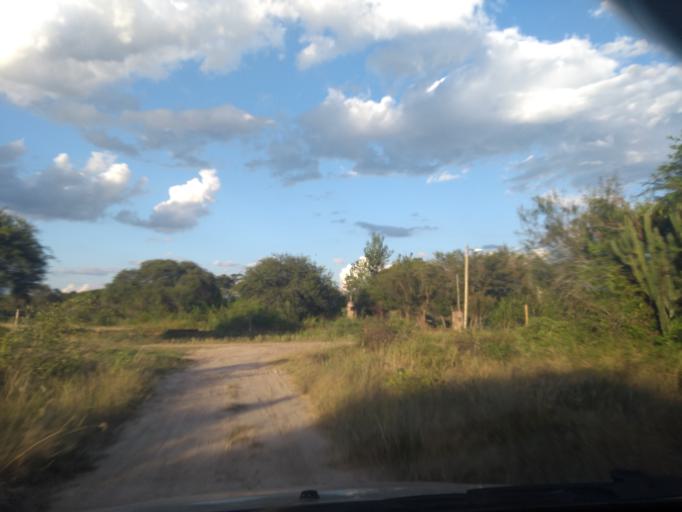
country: AR
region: Chaco
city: Colonia Benitez
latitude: -27.3902
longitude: -58.9426
